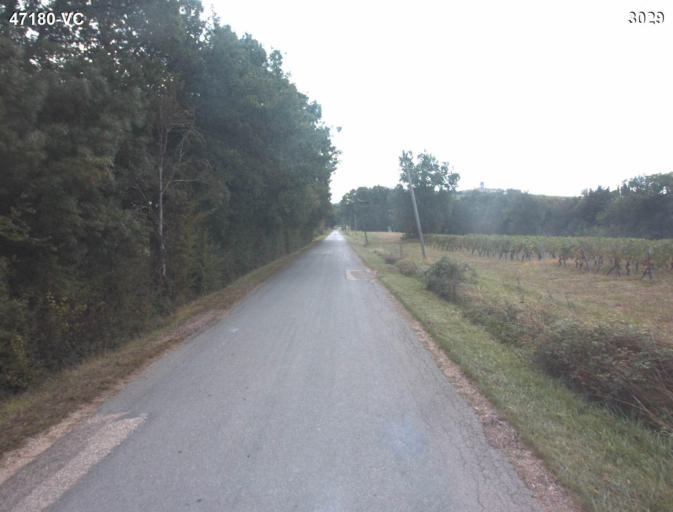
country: FR
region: Aquitaine
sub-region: Departement du Lot-et-Garonne
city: Sainte-Colombe-en-Bruilhois
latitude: 44.1693
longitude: 0.4521
